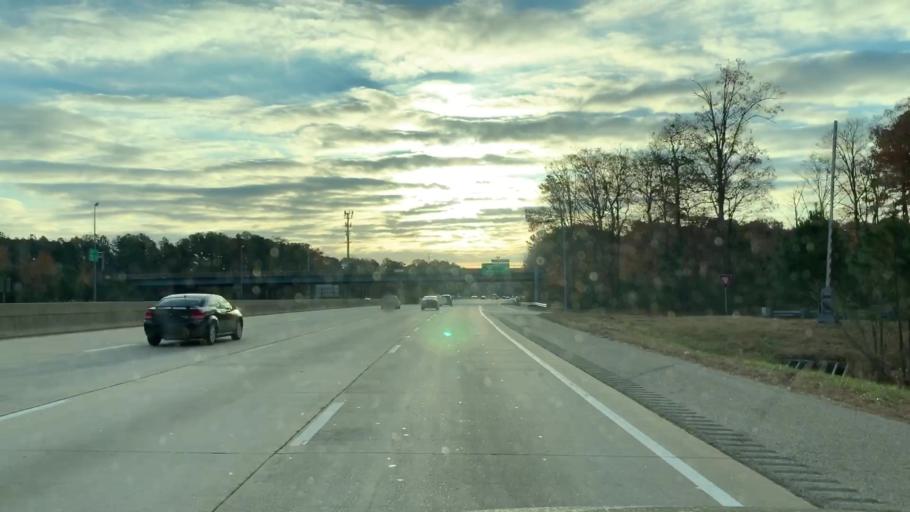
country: US
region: Virginia
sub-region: City of Poquoson
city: Poquoson
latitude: 37.1097
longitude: -76.4780
